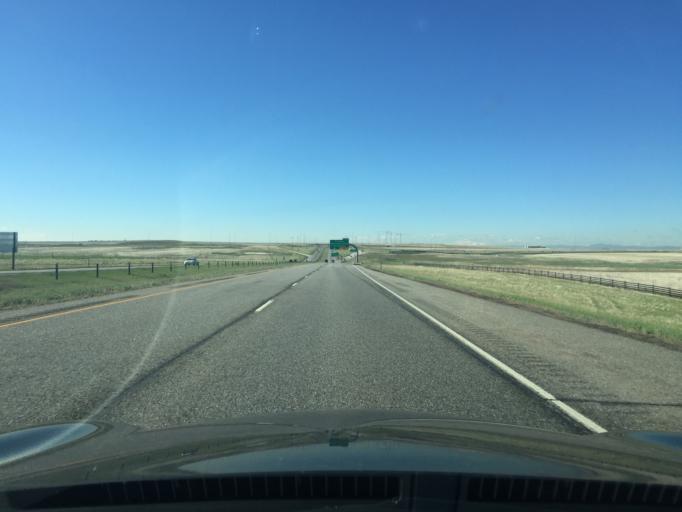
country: US
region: Colorado
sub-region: Adams County
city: Aurora
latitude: 39.8500
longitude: -104.7469
